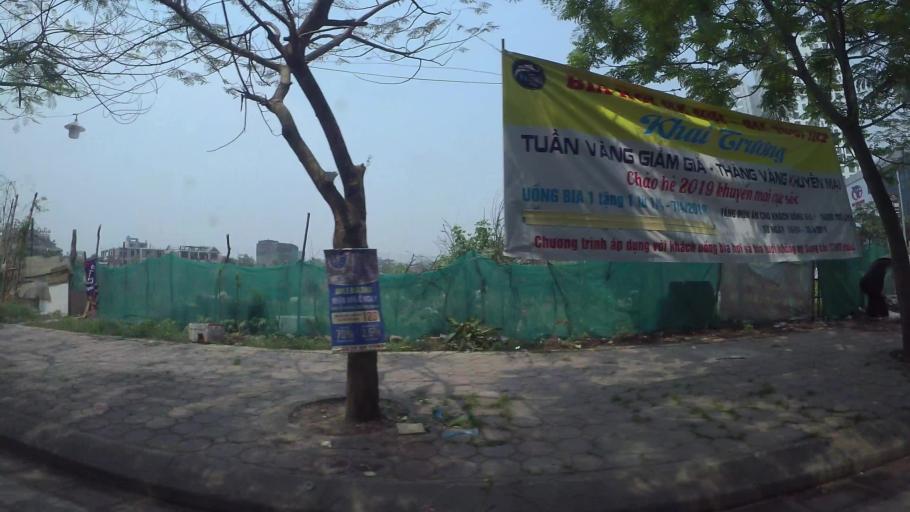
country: VN
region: Ha Noi
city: Van Dien
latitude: 20.9624
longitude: 105.8245
